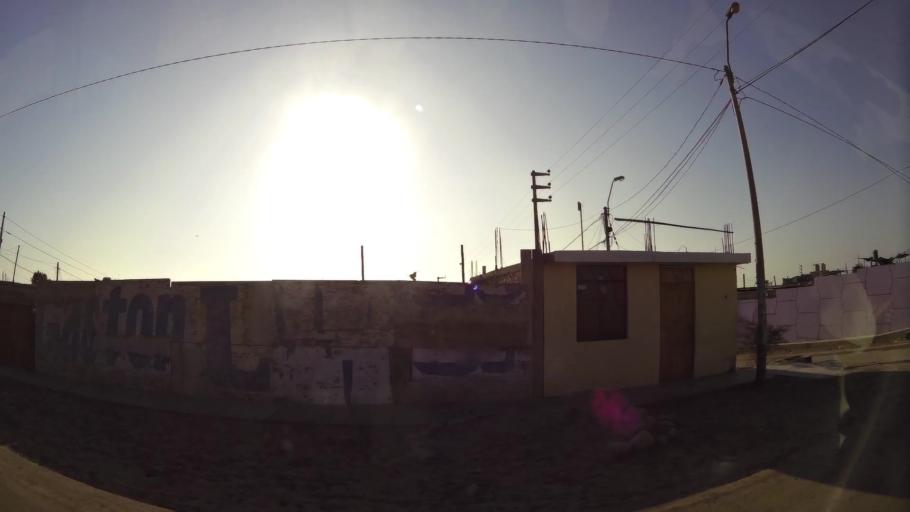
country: PE
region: Ica
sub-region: Provincia de Pisco
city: Villa Tupac Amaru
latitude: -13.7130
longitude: -76.1460
